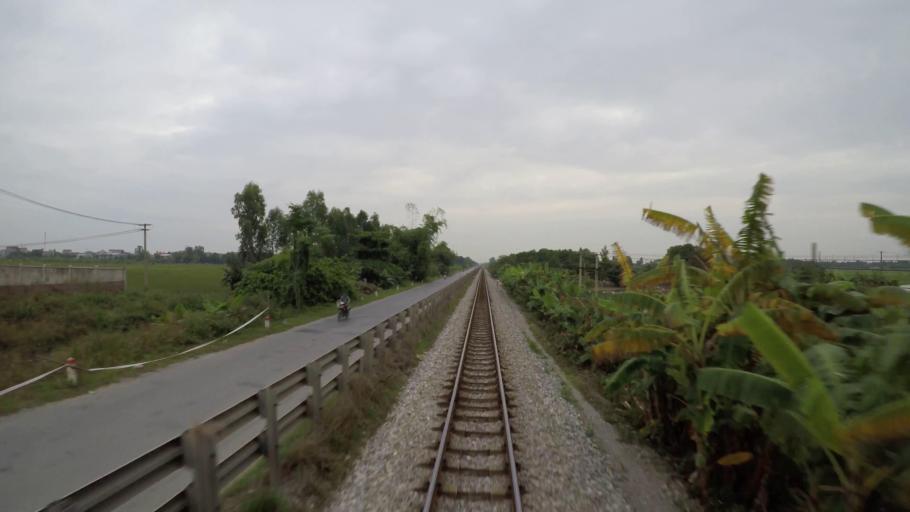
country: VN
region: Hung Yen
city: Ban Yen Nhan
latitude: 20.9853
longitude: 106.0608
